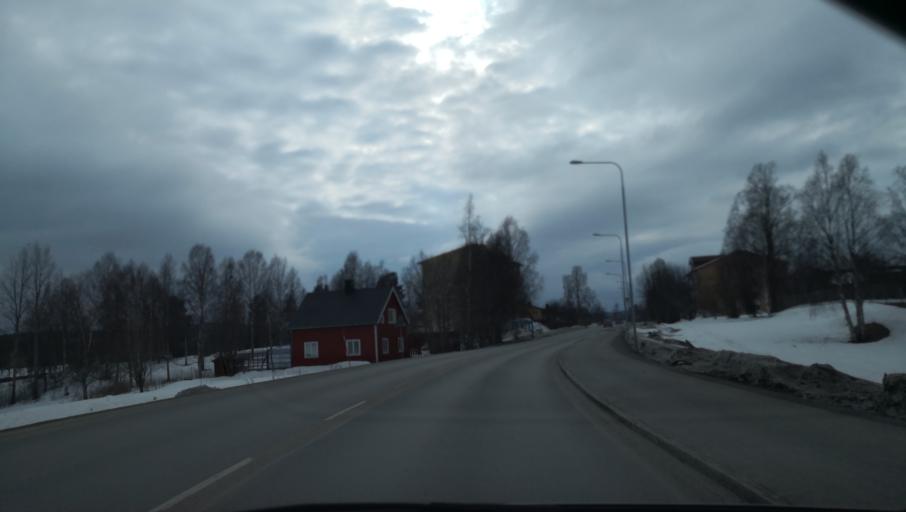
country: SE
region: Vaesterbotten
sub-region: Vannas Kommun
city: Vaennaes
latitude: 63.9082
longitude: 19.7698
